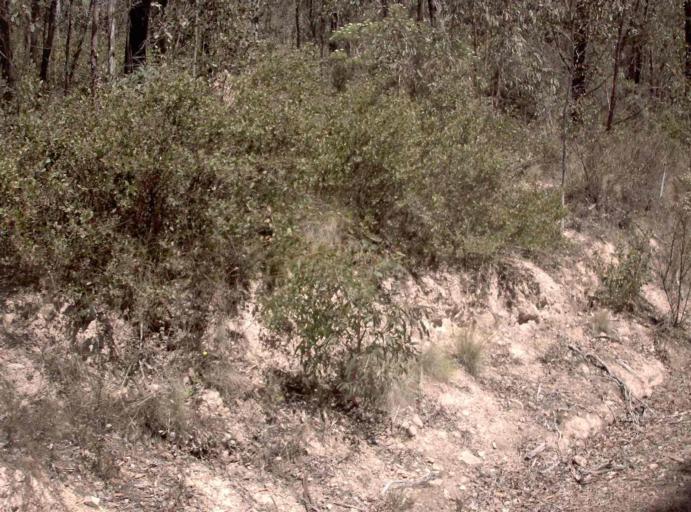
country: AU
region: New South Wales
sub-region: Snowy River
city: Jindabyne
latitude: -37.1076
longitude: 148.2507
